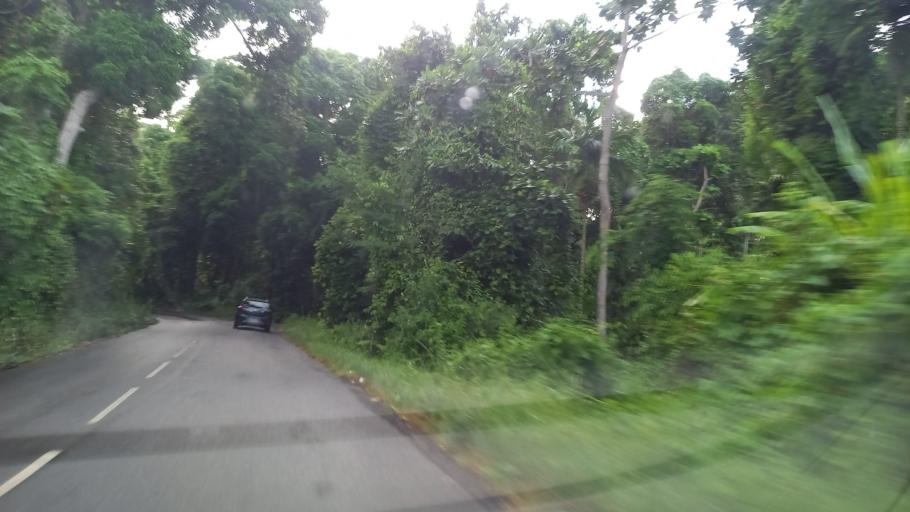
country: YT
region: Dembeni
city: Dembeni
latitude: -12.8385
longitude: 45.1642
